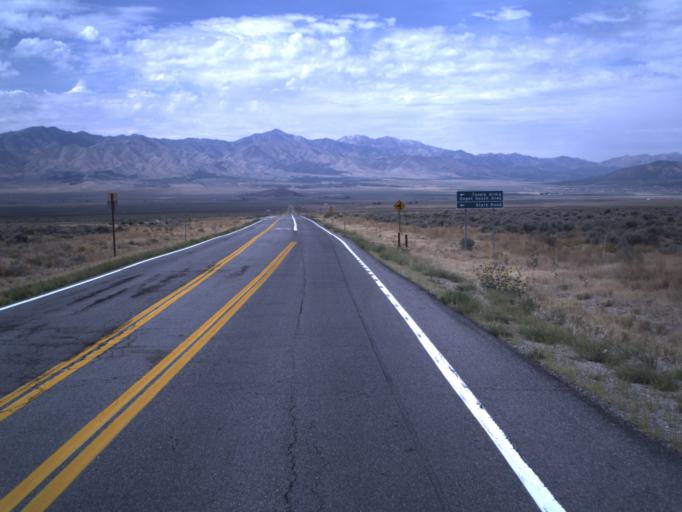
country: US
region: Utah
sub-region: Tooele County
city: Tooele
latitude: 40.3596
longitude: -112.3251
